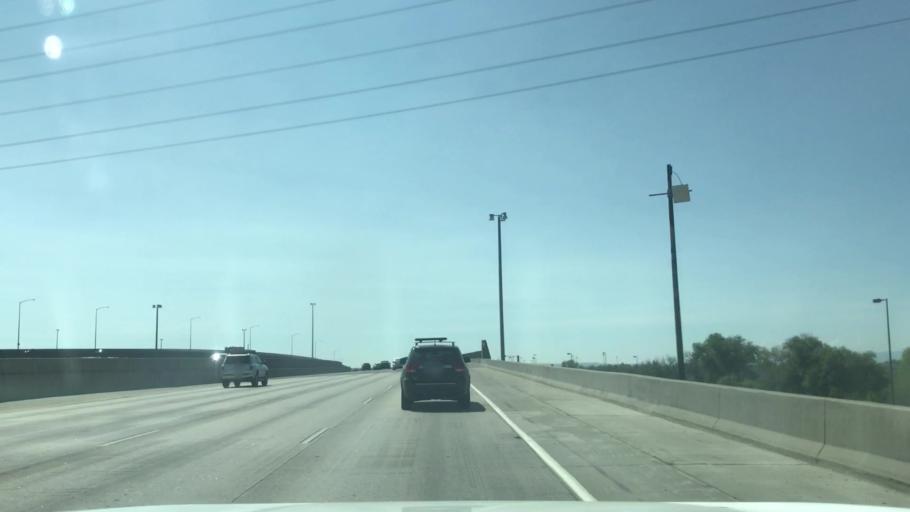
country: US
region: Colorado
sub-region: Denver County
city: Denver
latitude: 39.7079
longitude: -104.9980
